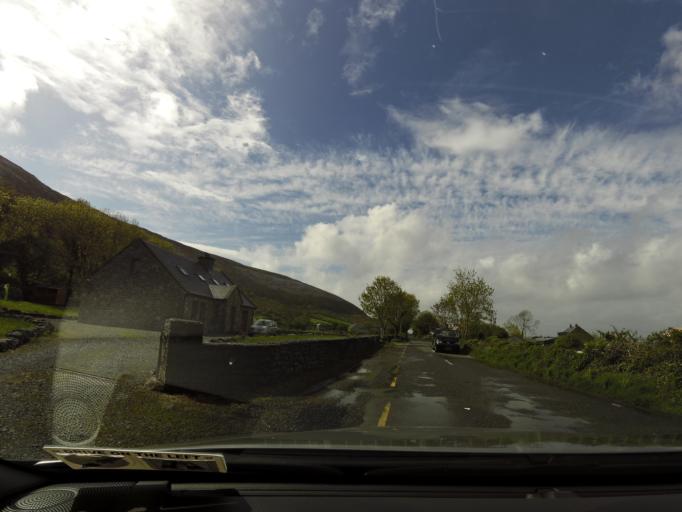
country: IE
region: Connaught
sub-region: County Galway
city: Bearna
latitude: 53.1387
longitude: -9.2225
